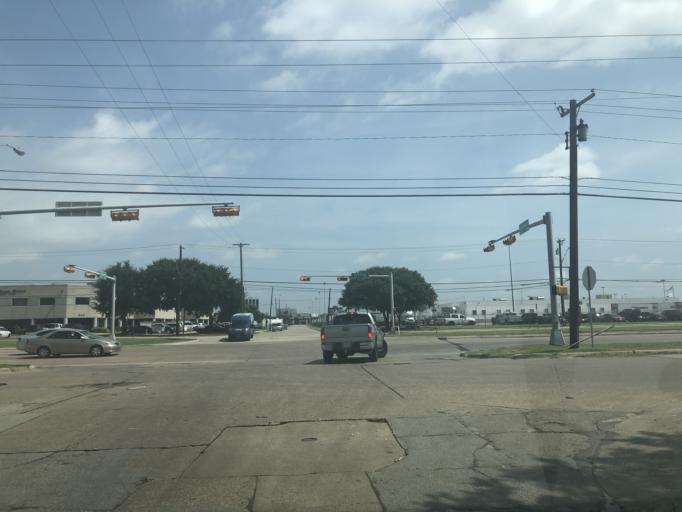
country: US
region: Texas
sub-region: Dallas County
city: Dallas
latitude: 32.8076
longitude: -96.8691
